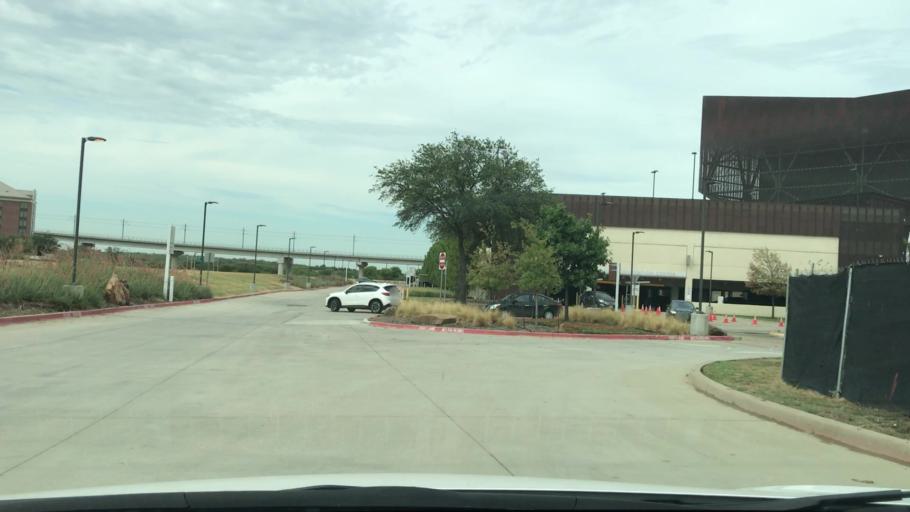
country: US
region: Texas
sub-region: Dallas County
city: Irving
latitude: 32.8769
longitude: -96.9448
